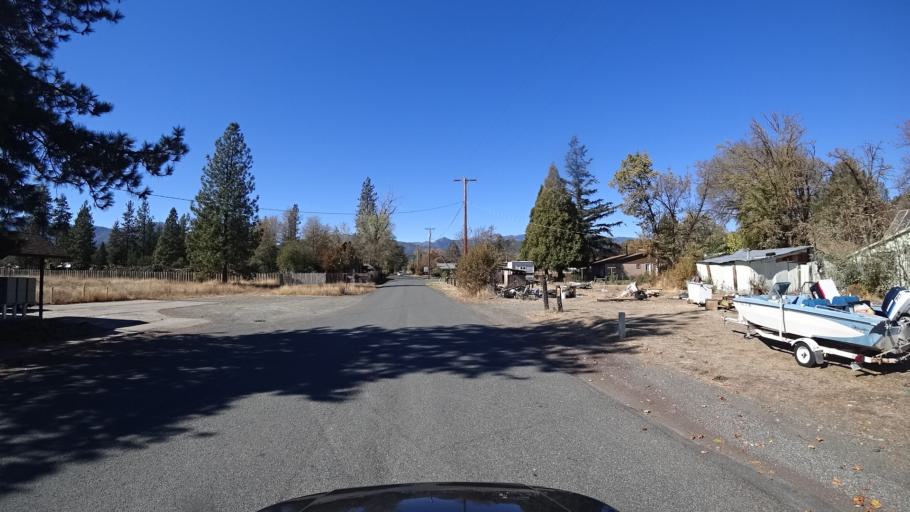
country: US
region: California
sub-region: Siskiyou County
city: Yreka
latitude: 41.5486
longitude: -122.9068
